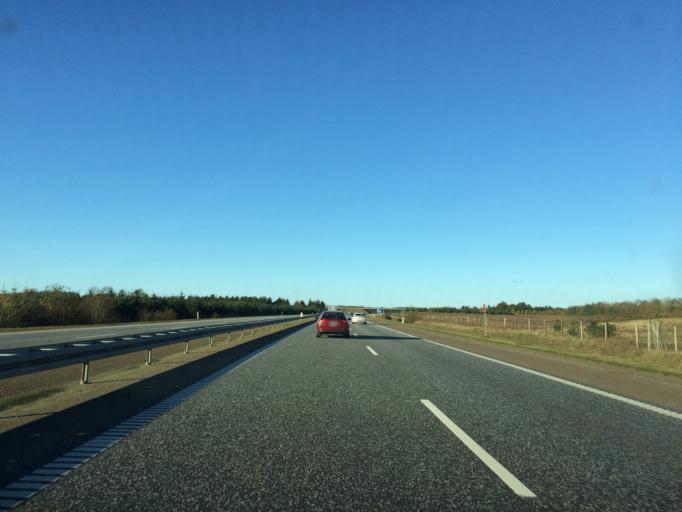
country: DK
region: Central Jutland
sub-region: Herning Kommune
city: Lind
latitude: 56.0242
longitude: 9.0105
